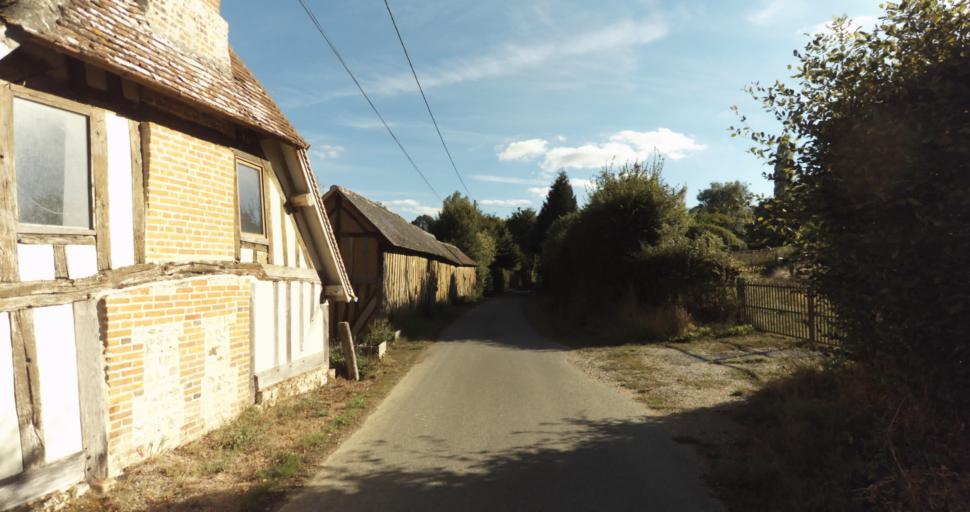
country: FR
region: Lower Normandy
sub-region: Departement de l'Orne
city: Vimoutiers
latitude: 48.9089
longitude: 0.1296
